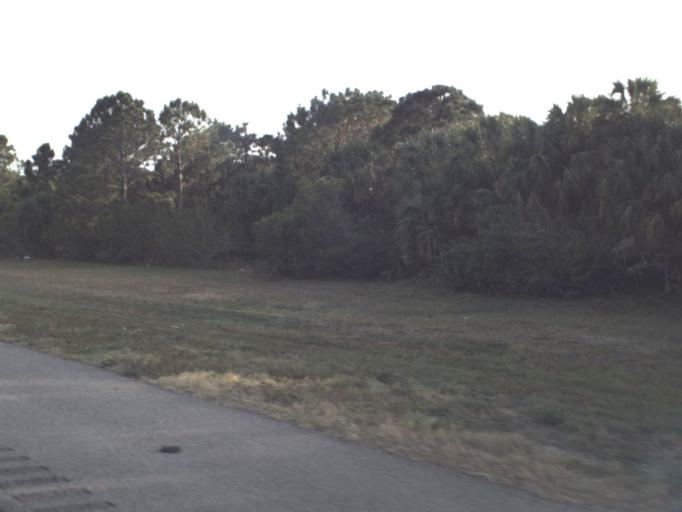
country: US
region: Florida
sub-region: Brevard County
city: Port Saint John
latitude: 28.4401
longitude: -80.8208
